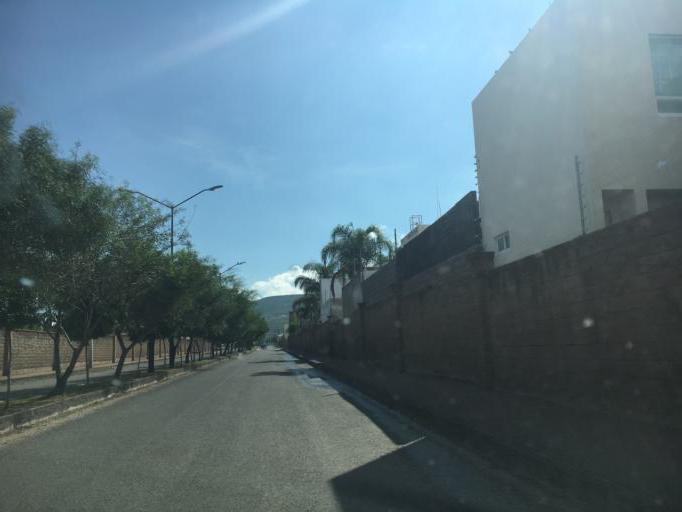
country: MX
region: Guanajuato
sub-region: Leon
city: Medina
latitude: 21.1285
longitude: -101.6195
